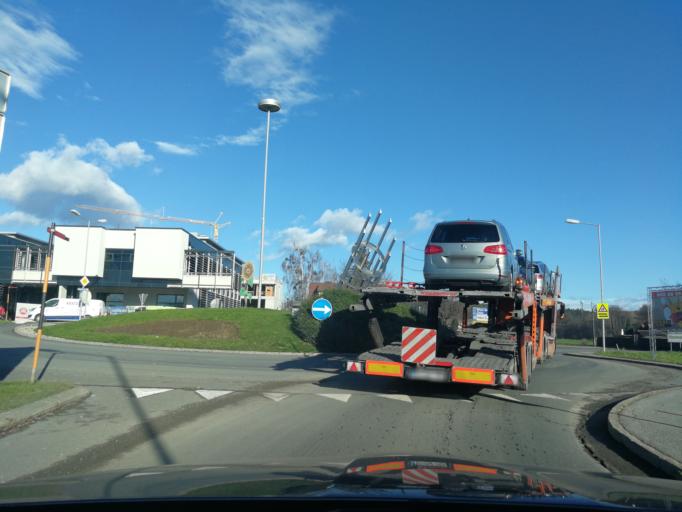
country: AT
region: Styria
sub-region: Politischer Bezirk Weiz
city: Gleisdorf
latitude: 47.0990
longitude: 15.7182
